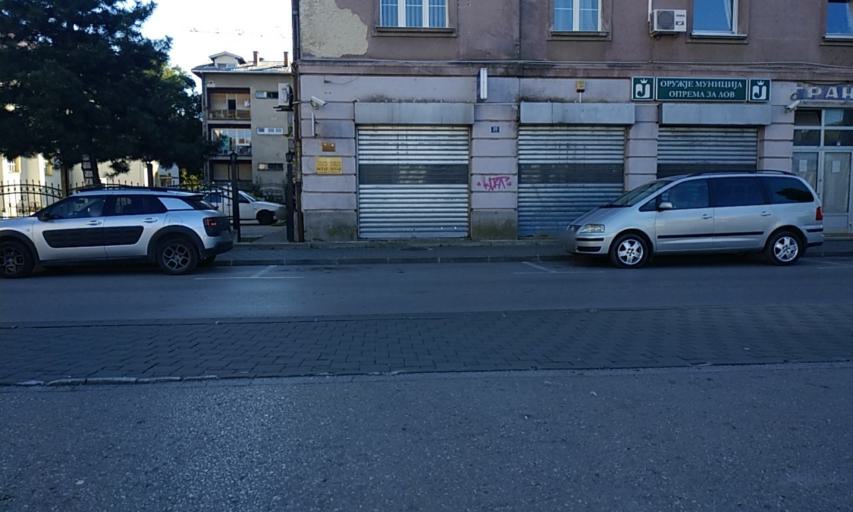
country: BA
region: Republika Srpska
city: Mejdan - Obilicevo
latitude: 44.7714
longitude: 17.1932
